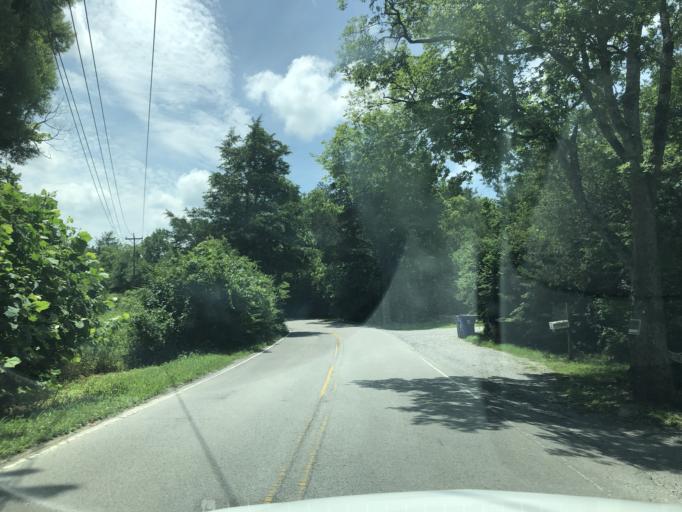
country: US
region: Tennessee
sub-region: Rutherford County
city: La Vergne
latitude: 36.0153
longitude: -86.6415
